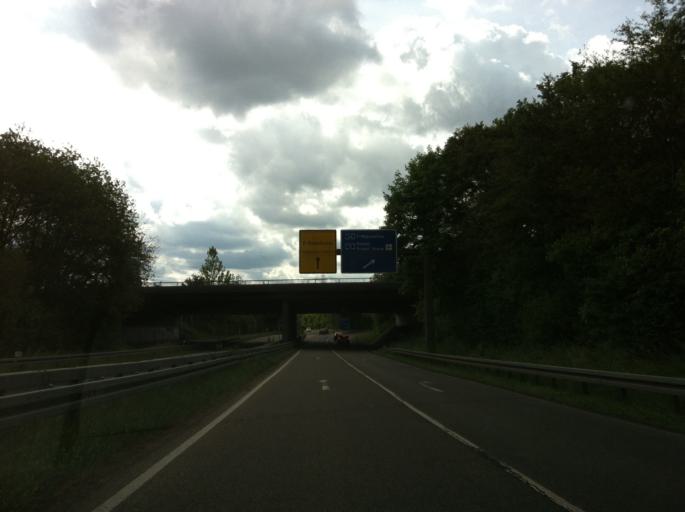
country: DE
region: Hesse
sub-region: Regierungsbezirk Darmstadt
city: Eschborn
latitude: 50.1347
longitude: 8.5849
